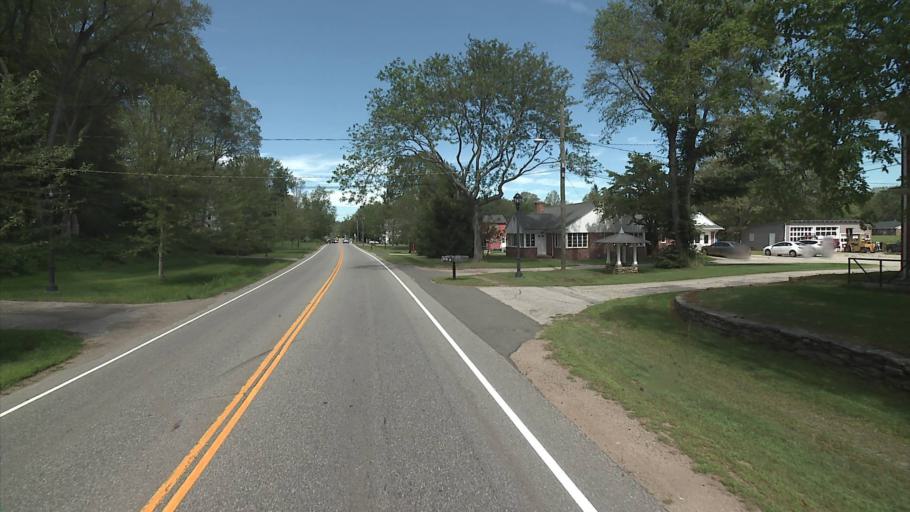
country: US
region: Connecticut
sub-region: Tolland County
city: Mansfield City
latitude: 41.7628
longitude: -72.1966
